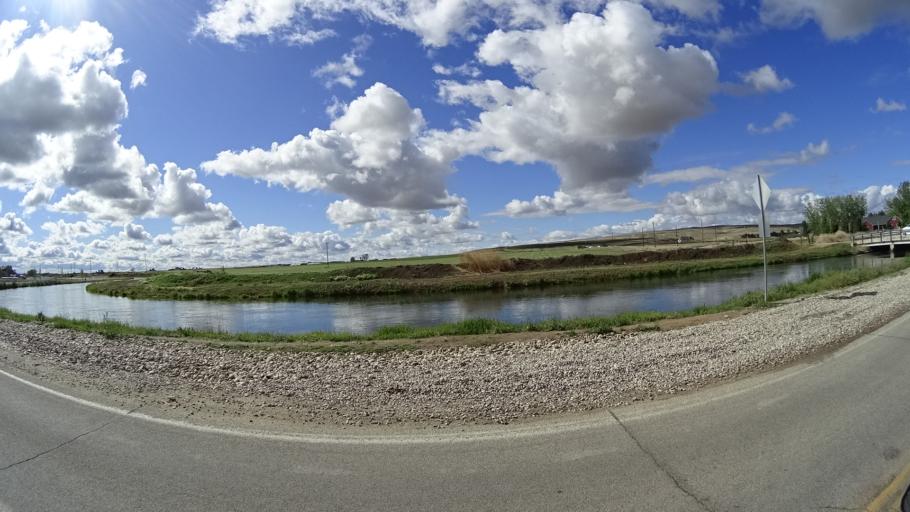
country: US
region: Idaho
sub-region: Ada County
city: Kuna
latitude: 43.4755
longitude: -116.4329
